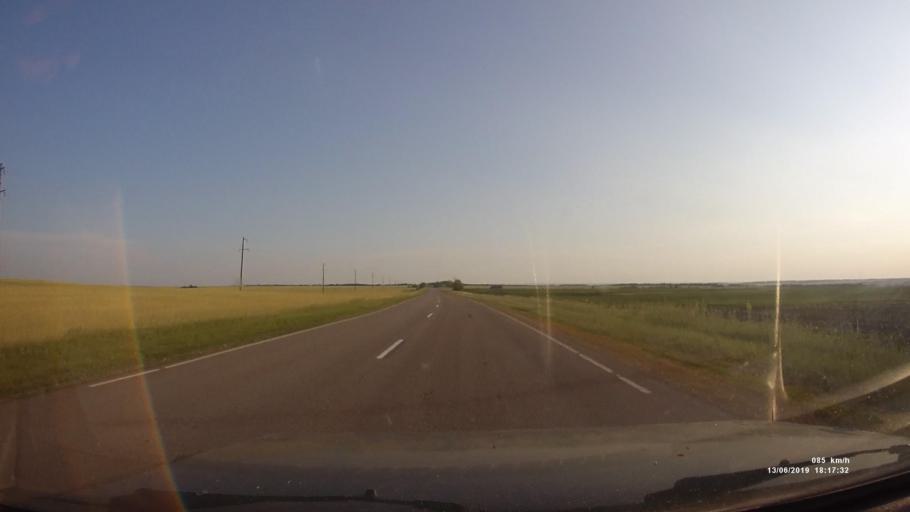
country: RU
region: Rostov
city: Kazanskaya
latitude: 49.9188
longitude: 41.3240
